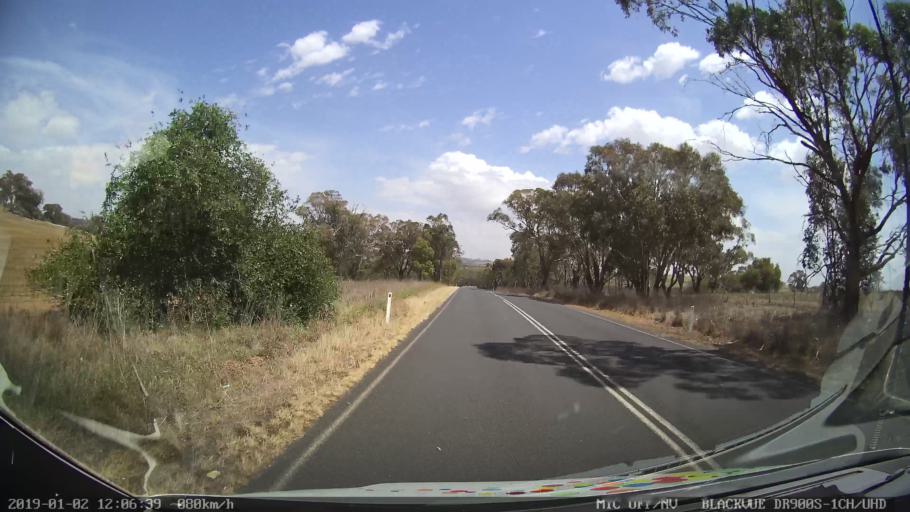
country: AU
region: New South Wales
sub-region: Young
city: Young
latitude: -34.5013
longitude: 148.2926
